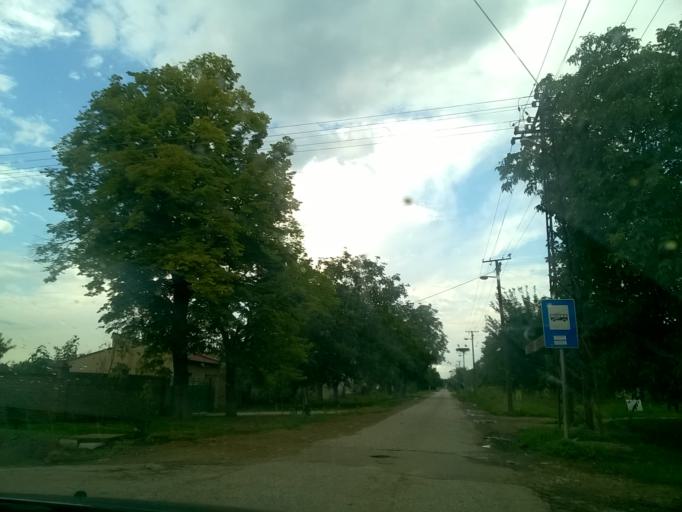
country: RS
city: Tomasevac
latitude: 45.2758
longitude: 20.6298
